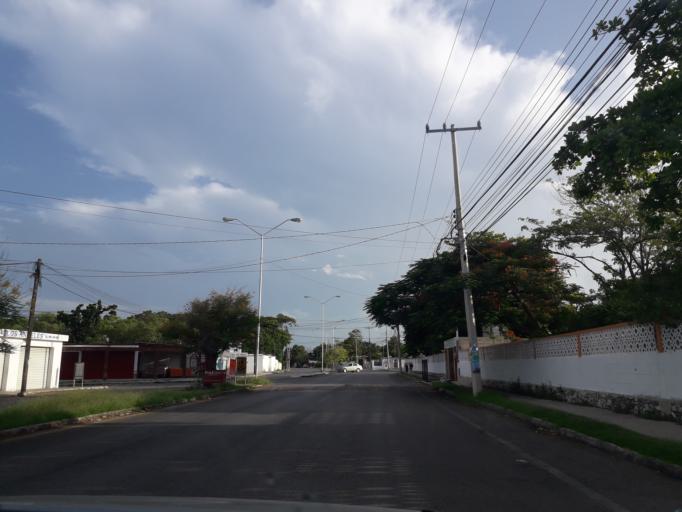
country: MX
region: Yucatan
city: Merida
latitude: 21.0219
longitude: -89.6311
